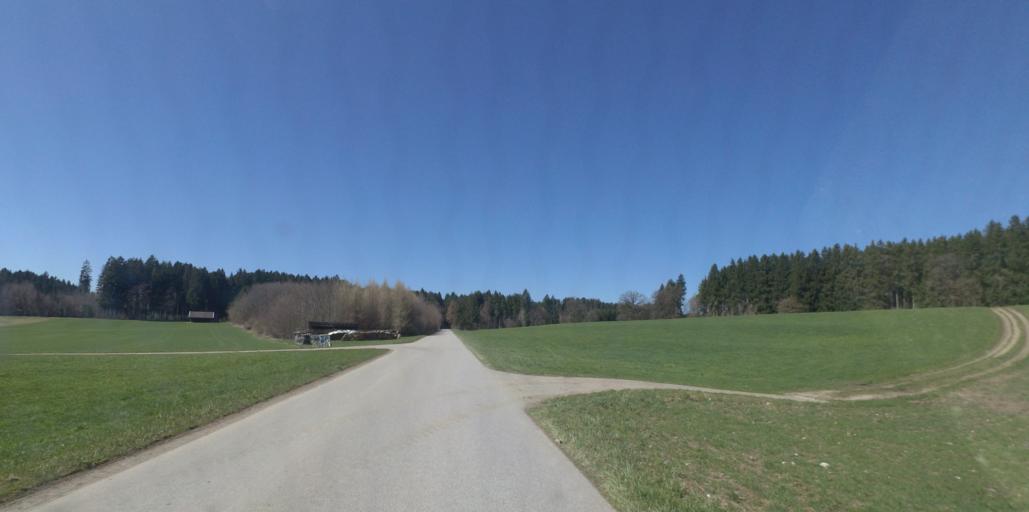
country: DE
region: Bavaria
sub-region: Upper Bavaria
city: Nussdorf
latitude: 47.8757
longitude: 12.5786
